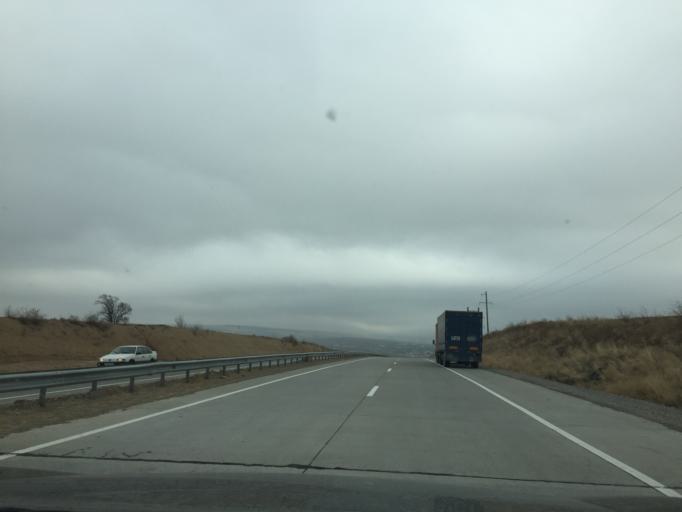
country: KZ
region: Ongtustik Qazaqstan
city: Sastobe
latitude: 42.5540
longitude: 70.1240
